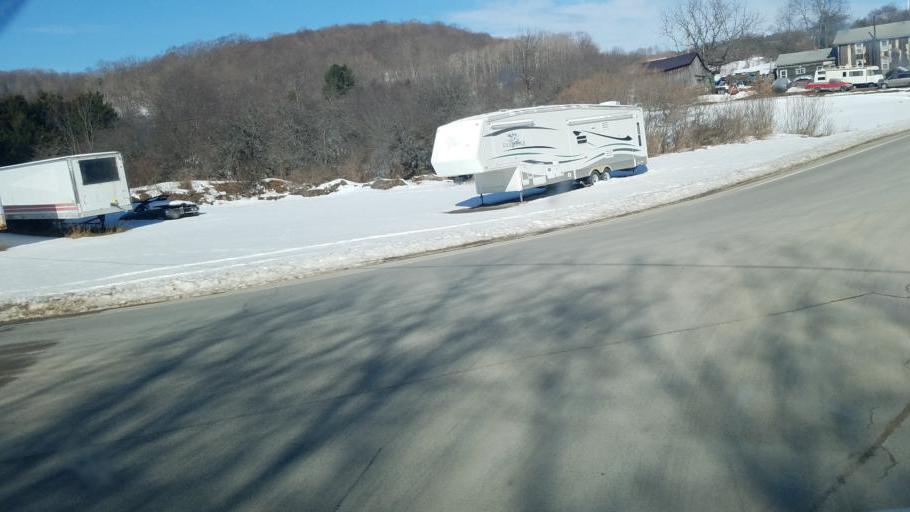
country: US
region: New York
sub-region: Allegany County
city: Andover
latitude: 42.0881
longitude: -77.7813
